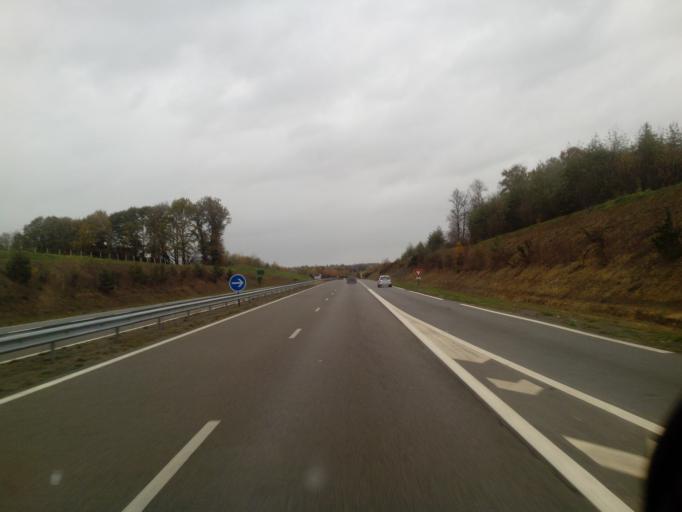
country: FR
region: Brittany
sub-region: Departement d'Ille-et-Vilaine
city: Betton
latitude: 48.1810
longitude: -1.6248
